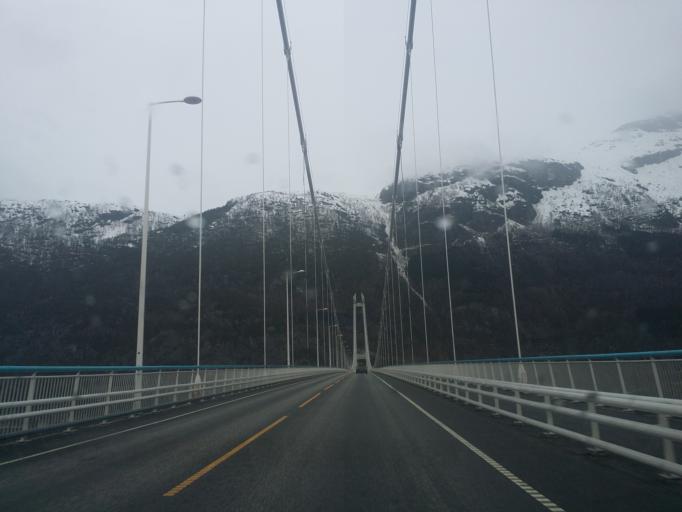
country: NO
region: Hordaland
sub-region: Ulvik
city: Ulvik
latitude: 60.4754
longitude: 6.8341
